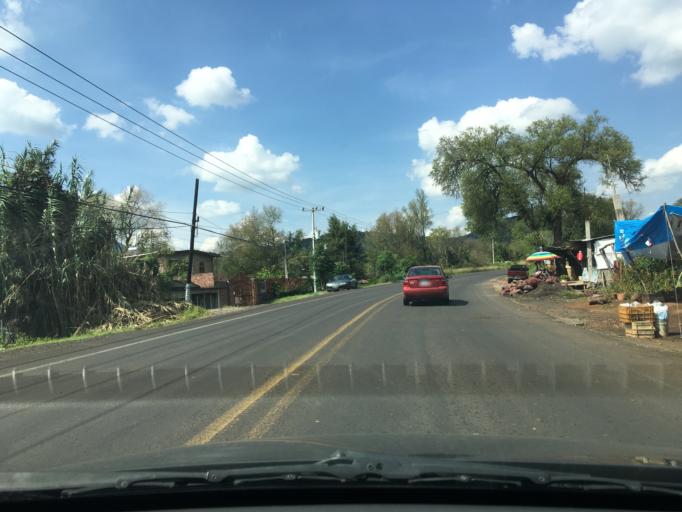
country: MX
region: Michoacan
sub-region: Tingueindin
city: Tingueindin
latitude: 19.7988
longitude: -102.5199
